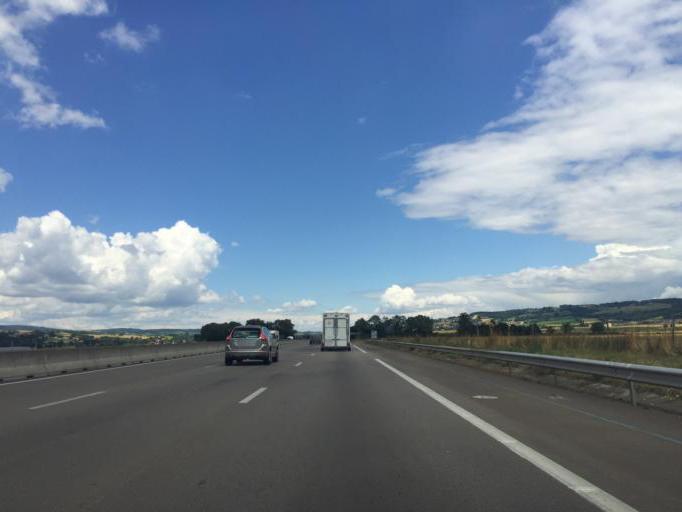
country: FR
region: Rhone-Alpes
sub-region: Departement de l'Isere
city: Auberives-sur-Vareze
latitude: 45.4419
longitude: 4.8266
